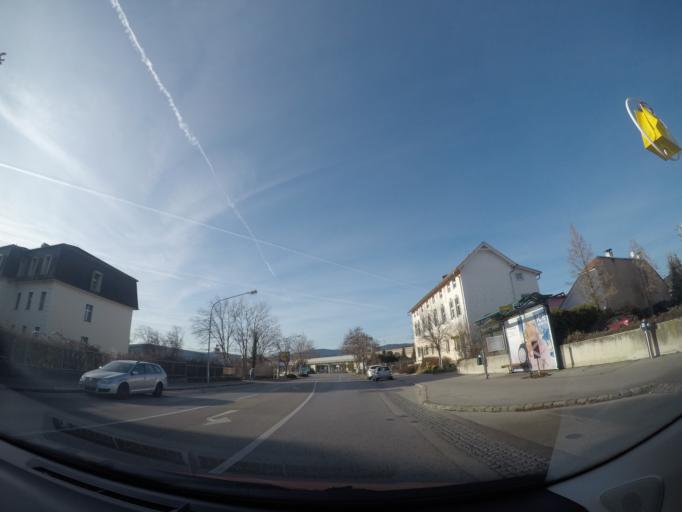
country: AT
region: Lower Austria
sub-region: Politischer Bezirk Baden
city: Pfaffstatten
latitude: 48.0133
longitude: 16.2547
